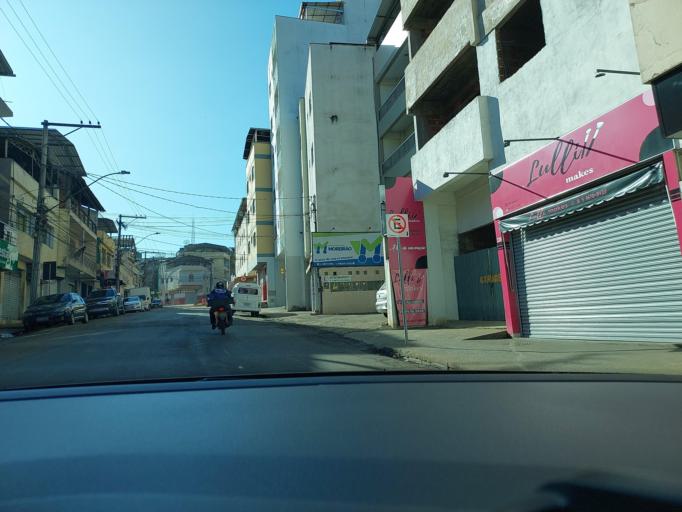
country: BR
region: Minas Gerais
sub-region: Ponte Nova
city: Ponte Nova
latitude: -20.4065
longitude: -42.8945
